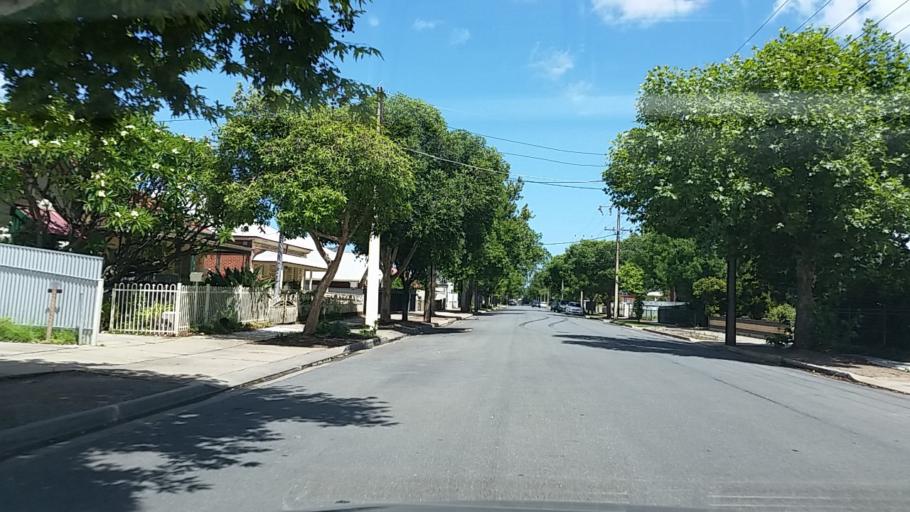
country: AU
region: South Australia
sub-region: City of West Torrens
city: Thebarton
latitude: -34.9268
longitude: 138.5658
